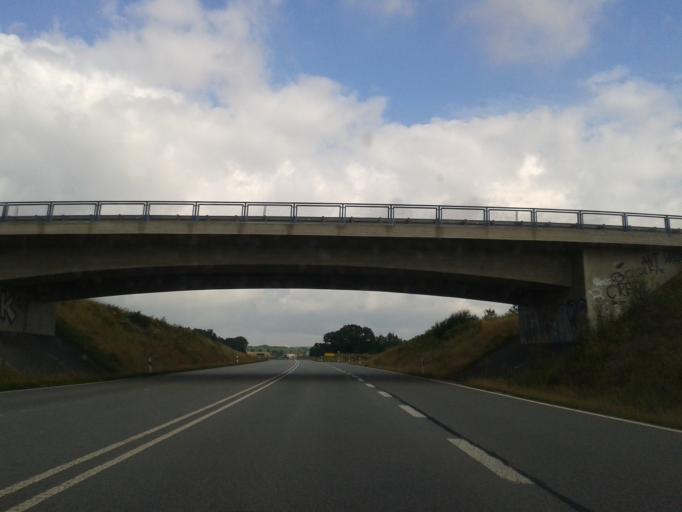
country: DE
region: Saxony
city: Radeberg
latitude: 51.1029
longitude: 13.9390
